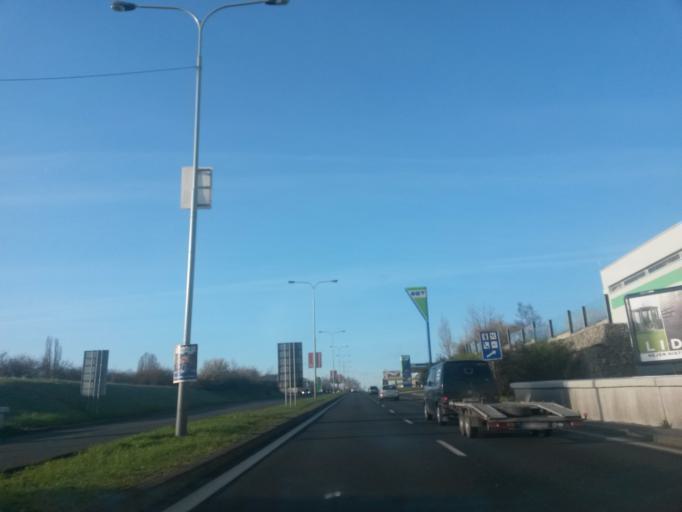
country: CZ
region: Praha
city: Branik
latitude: 50.0323
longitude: 14.3818
